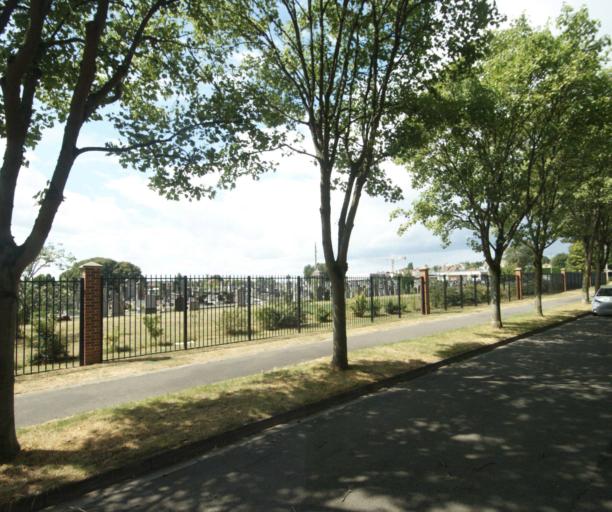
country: FR
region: Nord-Pas-de-Calais
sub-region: Departement du Nord
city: Croix
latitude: 50.6814
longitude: 3.1503
